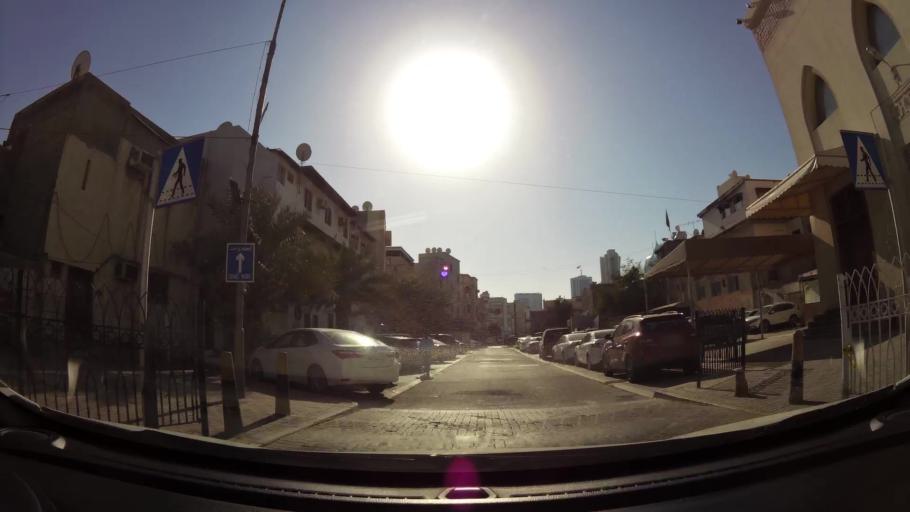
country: BH
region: Manama
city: Manama
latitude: 26.2370
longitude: 50.5861
